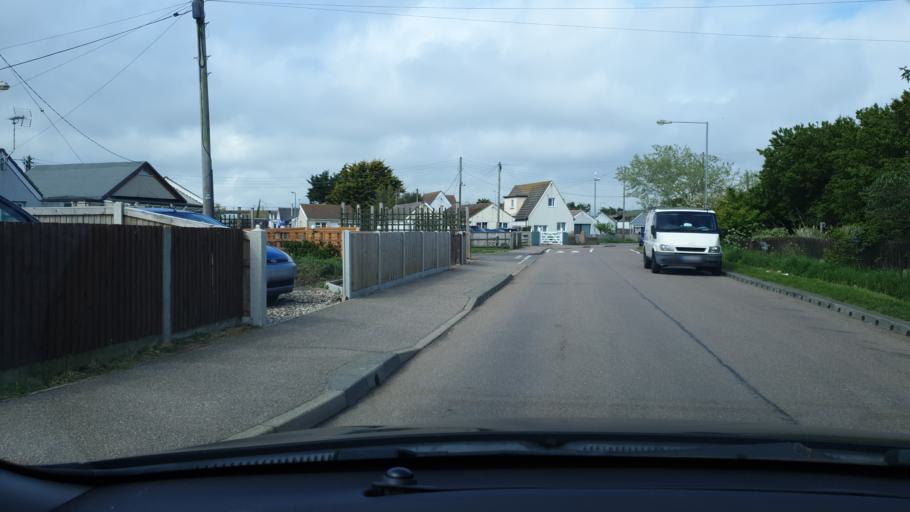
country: GB
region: England
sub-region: Essex
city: Saint Osyth
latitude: 51.7735
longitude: 1.1004
